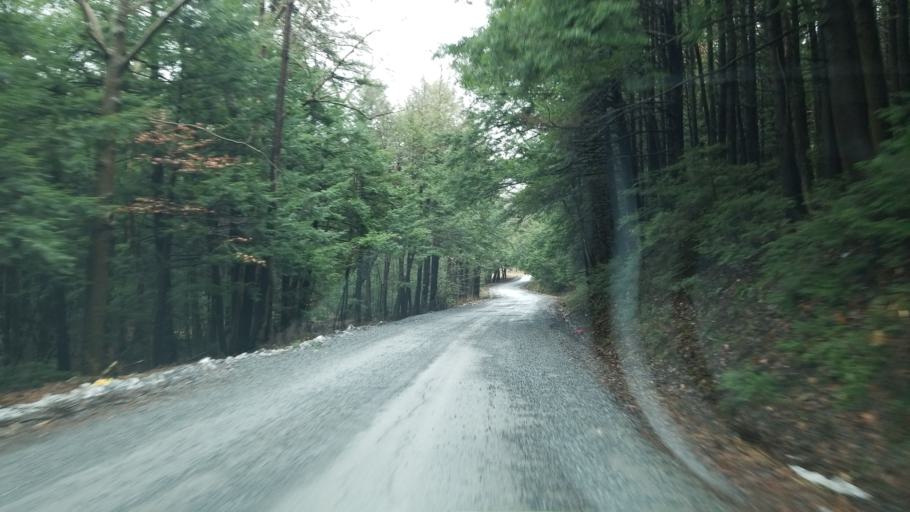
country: US
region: Pennsylvania
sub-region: Clearfield County
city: DuBois
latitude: 41.0803
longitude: -78.6634
